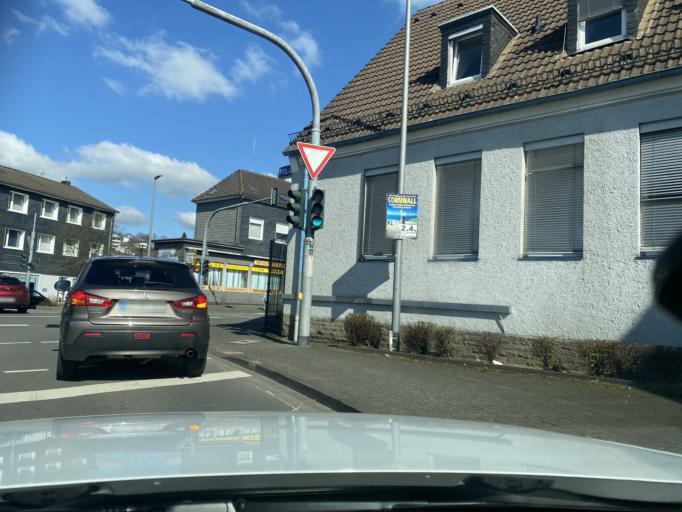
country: DE
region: North Rhine-Westphalia
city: Wipperfurth
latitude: 51.1182
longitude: 7.4001
